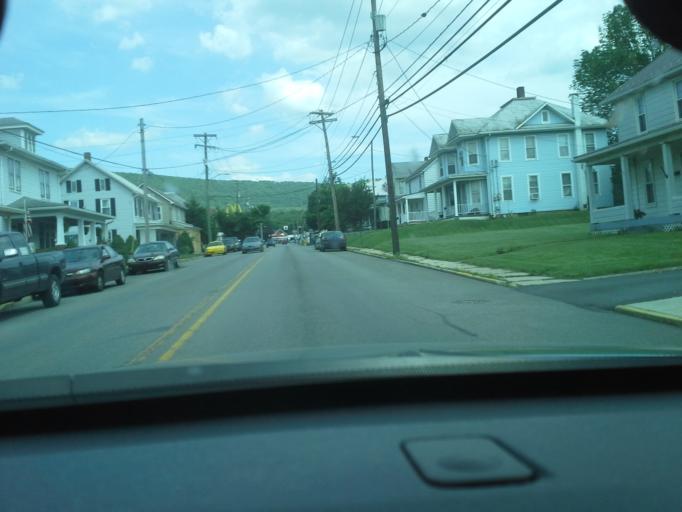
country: US
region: Pennsylvania
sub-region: Fulton County
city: McConnellsburg
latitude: 39.9304
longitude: -77.9929
